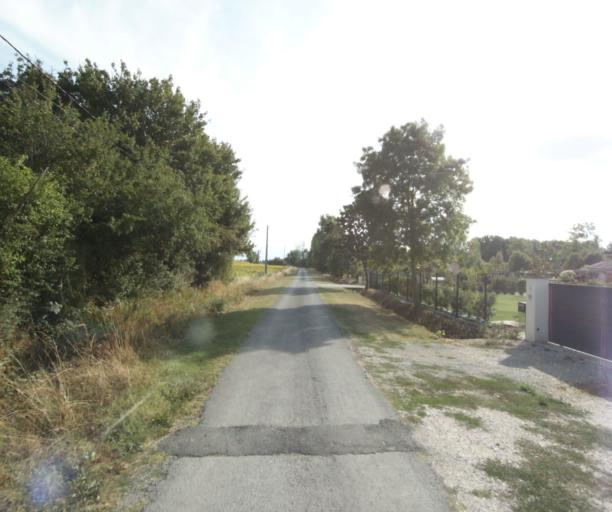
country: FR
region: Midi-Pyrenees
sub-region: Departement du Tarn
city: Puylaurens
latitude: 43.5186
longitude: 2.0007
